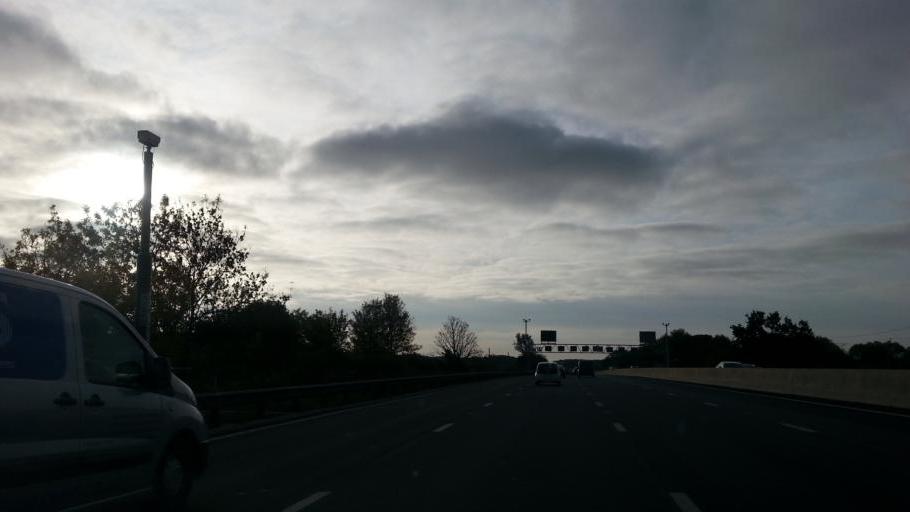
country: GB
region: England
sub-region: Northamptonshire
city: Long Buckby
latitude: 52.2852
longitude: -1.1020
